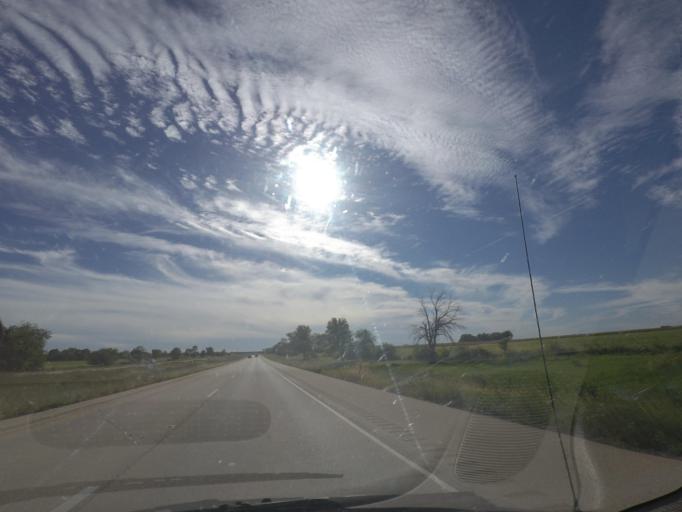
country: US
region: Illinois
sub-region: Macon County
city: Forsyth
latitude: 39.9245
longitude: -88.8525
